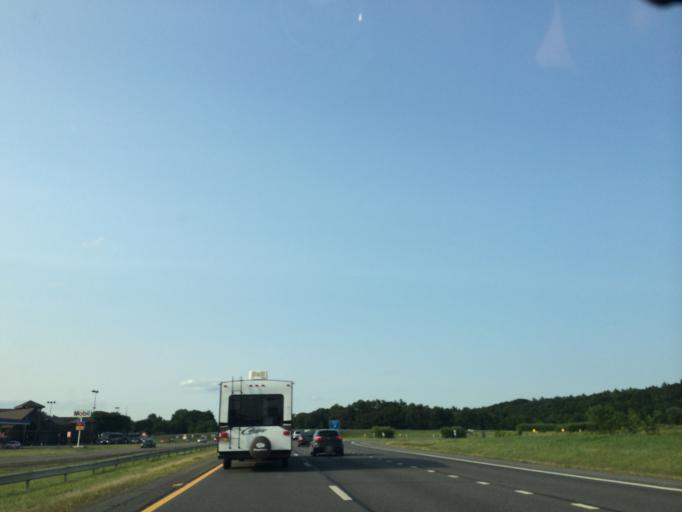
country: US
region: New York
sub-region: Albany County
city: Ravena
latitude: 42.4257
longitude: -73.8056
